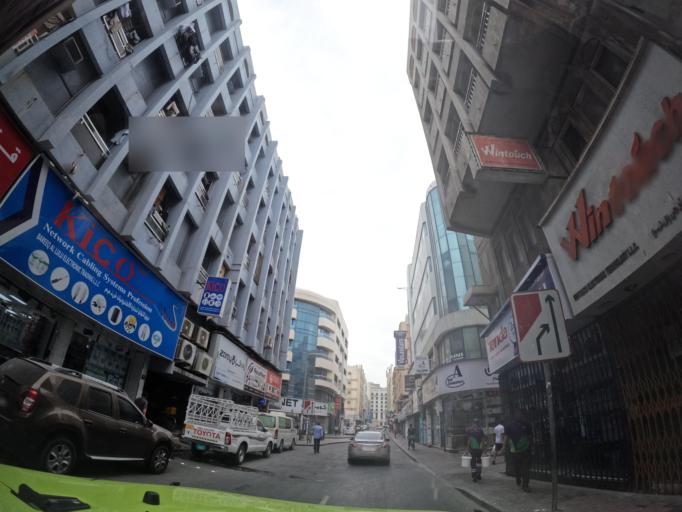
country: AE
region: Ash Shariqah
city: Sharjah
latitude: 25.2616
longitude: 55.2918
